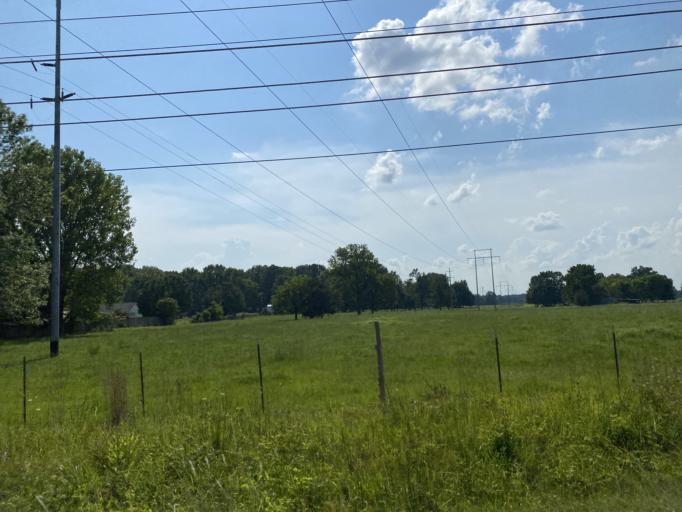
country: US
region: Alabama
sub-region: Lawrence County
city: Town Creek
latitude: 34.6605
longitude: -87.4057
